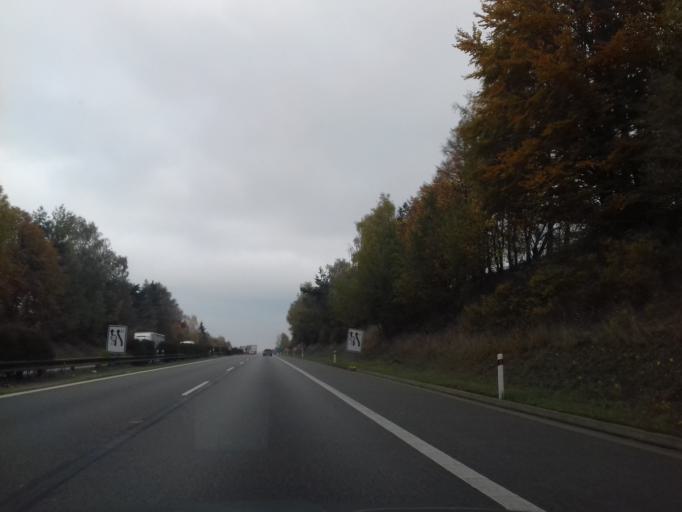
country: CZ
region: Central Bohemia
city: Trhovy Stepanov
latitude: 49.7196
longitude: 15.0514
